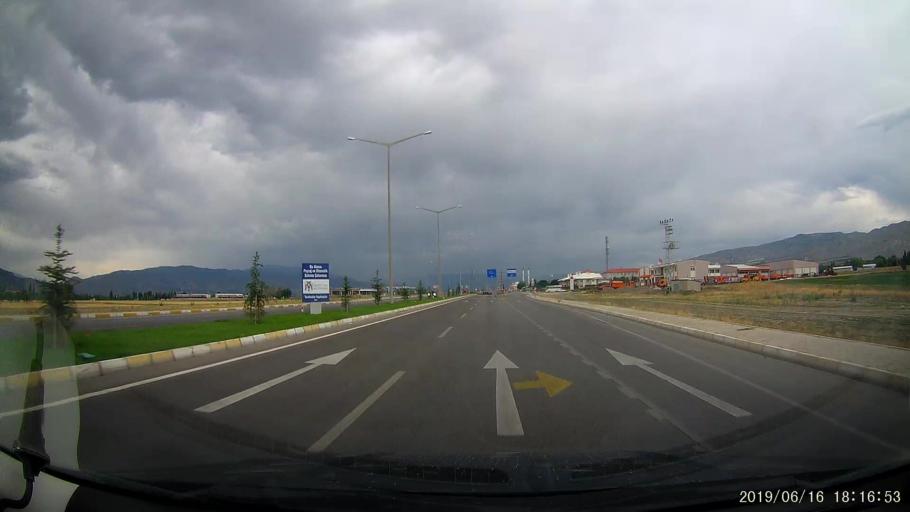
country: TR
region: Erzincan
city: Erzincan
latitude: 39.7312
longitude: 39.5410
